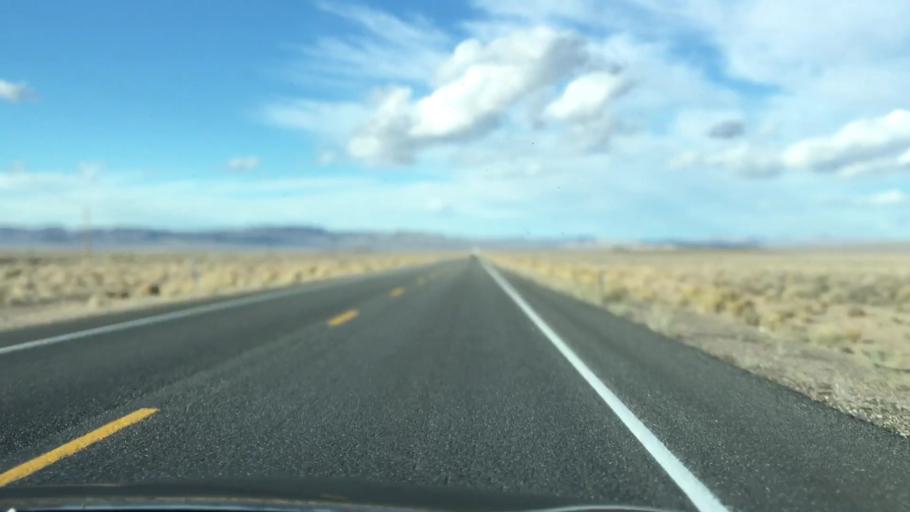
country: US
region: Nevada
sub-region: Esmeralda County
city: Goldfield
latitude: 37.4005
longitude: -117.1487
